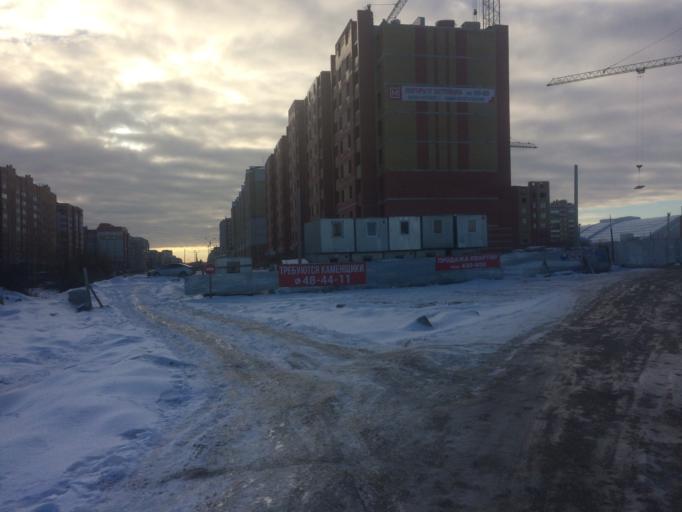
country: RU
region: Mariy-El
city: Yoshkar-Ola
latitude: 56.6426
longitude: 47.9257
